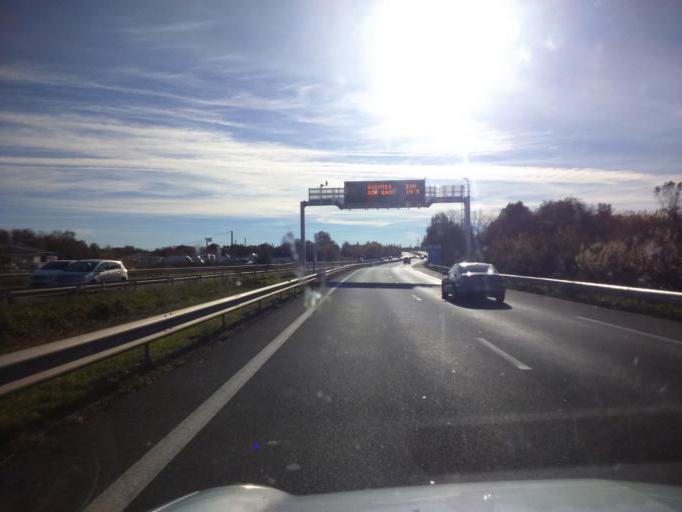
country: FR
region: Poitou-Charentes
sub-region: Departement de la Charente-Maritime
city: Breuil-Magne
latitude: 45.9733
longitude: -0.9889
